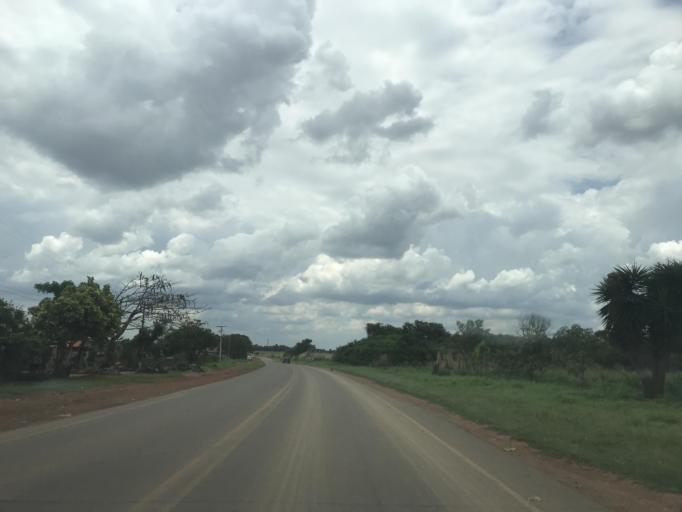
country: BR
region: Goias
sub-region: Vianopolis
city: Vianopolis
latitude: -16.7364
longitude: -48.4960
